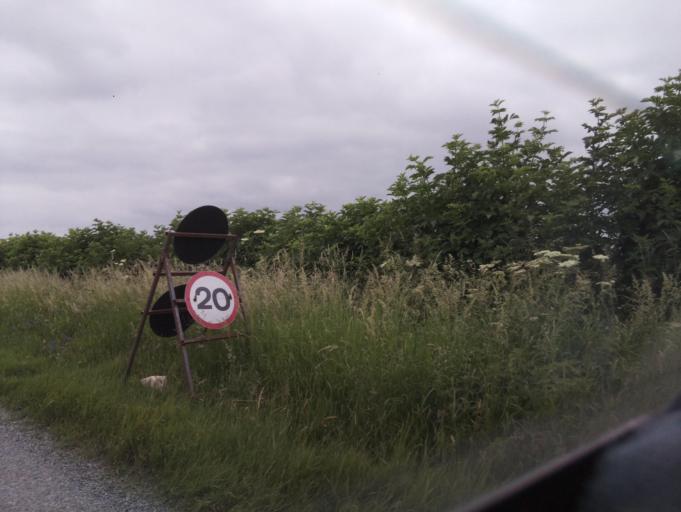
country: GB
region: England
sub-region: District of Rutland
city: Exton
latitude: 52.6719
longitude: -0.6486
